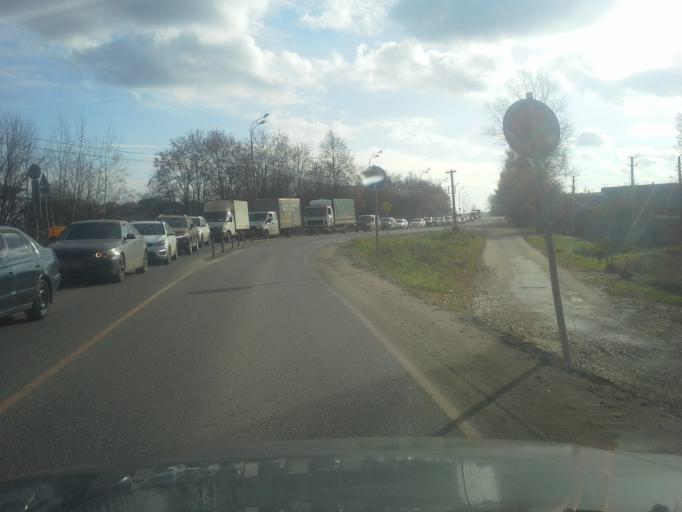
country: RU
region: Moskovskaya
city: Zvenigorod
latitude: 55.6995
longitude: 36.8832
